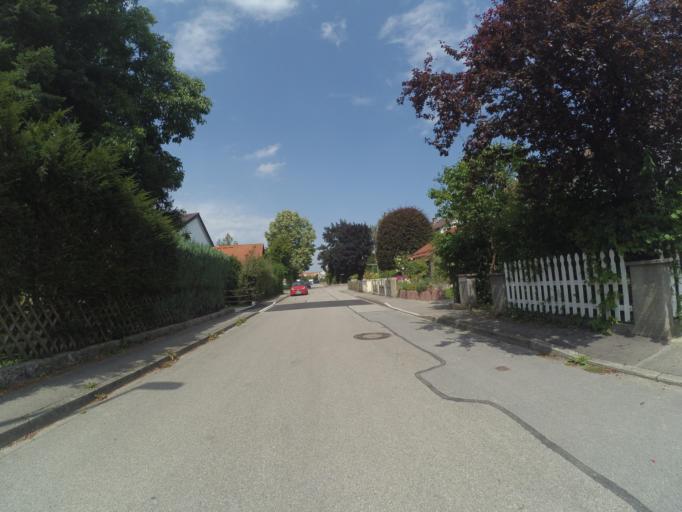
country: DE
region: Bavaria
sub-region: Swabia
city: Buchloe
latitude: 48.0362
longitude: 10.7130
